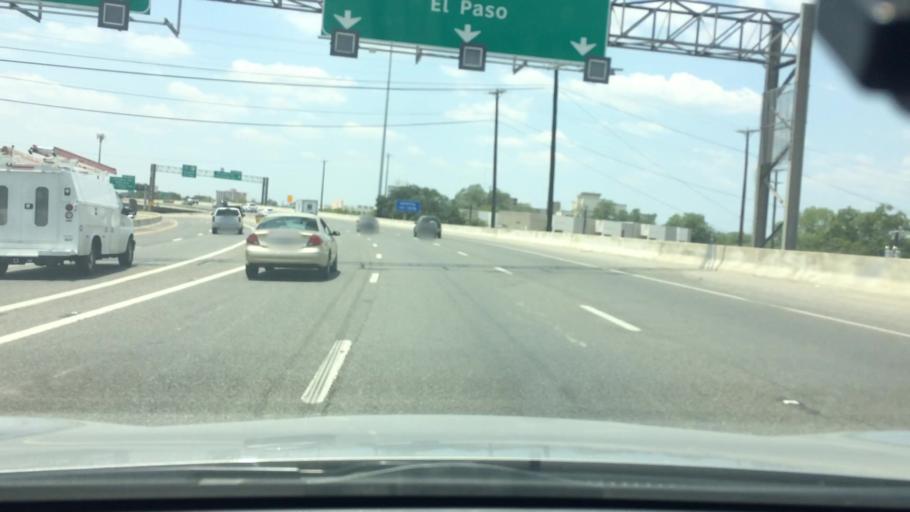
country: US
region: Texas
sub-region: Bexar County
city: San Antonio
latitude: 29.4408
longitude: -98.4873
